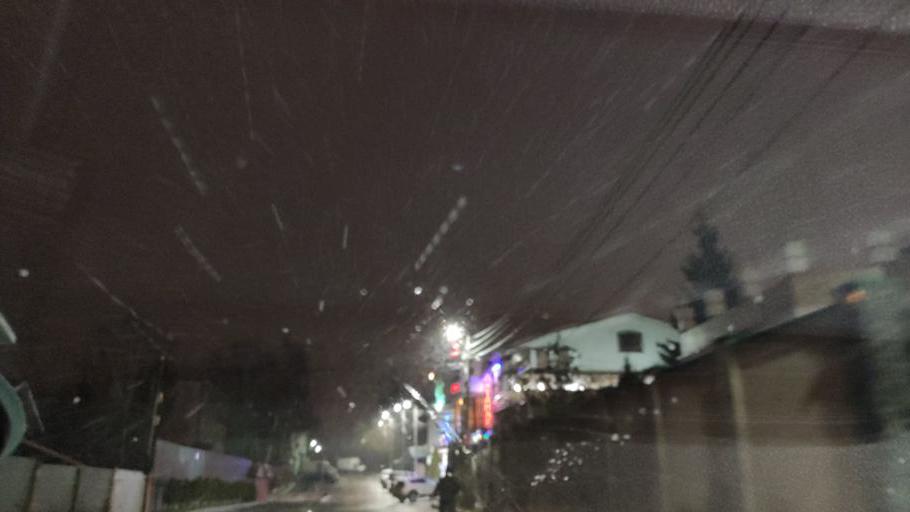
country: RU
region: Moskovskaya
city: Novoivanovskoye
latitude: 55.7137
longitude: 37.3745
